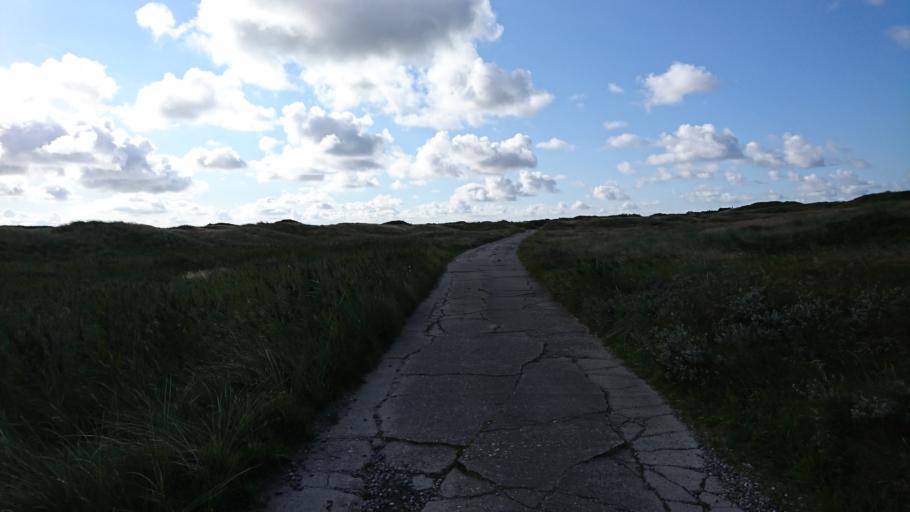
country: DK
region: South Denmark
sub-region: Fano Kommune
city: Nordby
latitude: 55.4473
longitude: 8.3602
